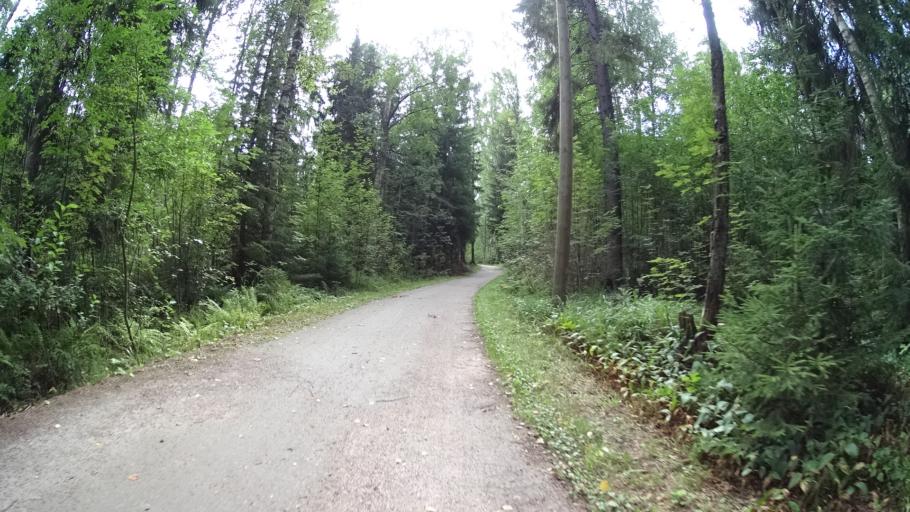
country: FI
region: Uusimaa
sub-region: Helsinki
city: Helsinki
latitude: 60.2620
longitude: 24.9029
